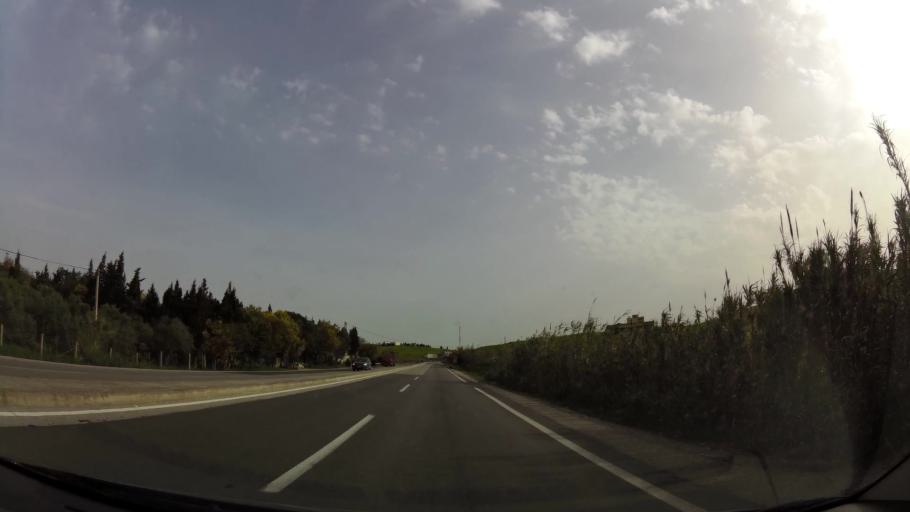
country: MA
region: Tanger-Tetouan
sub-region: Tanger-Assilah
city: Dar Chaoui
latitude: 35.6695
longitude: -5.6982
